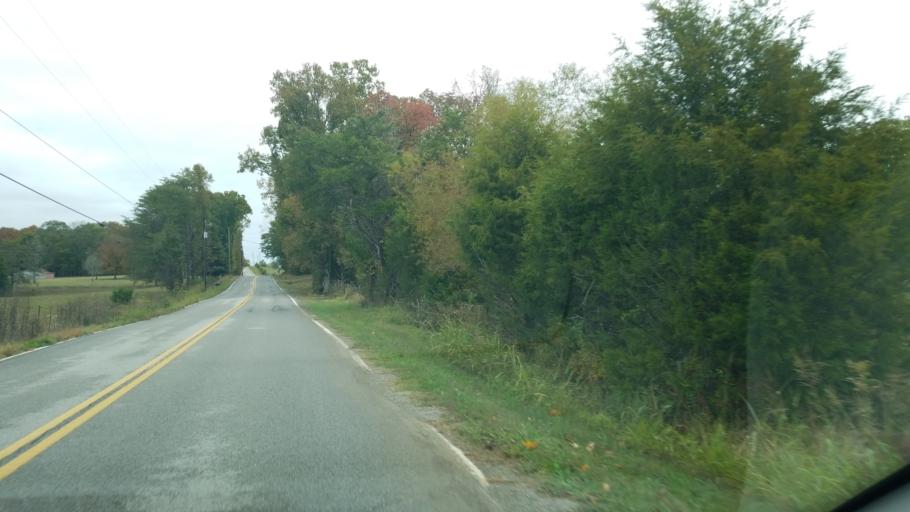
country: US
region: Tennessee
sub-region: Bradley County
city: Hopewell
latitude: 35.2652
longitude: -84.9729
